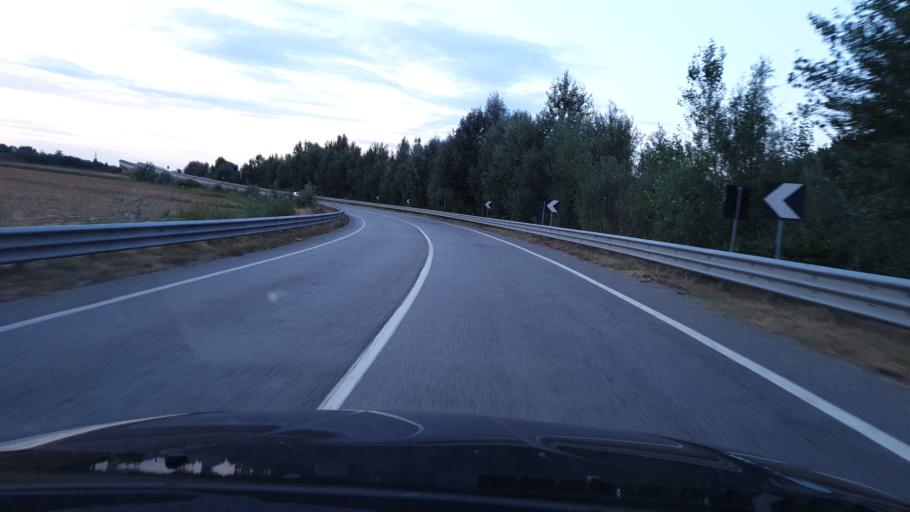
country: IT
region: Emilia-Romagna
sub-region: Provincia di Ravenna
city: Alfonsine
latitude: 44.5018
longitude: 12.0617
